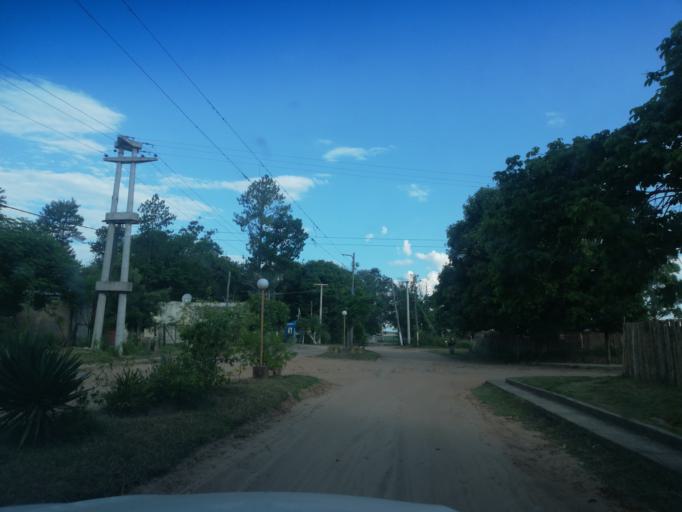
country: AR
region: Corrientes
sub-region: Departamento de San Miguel
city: San Miguel
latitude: -28.0011
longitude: -57.5932
